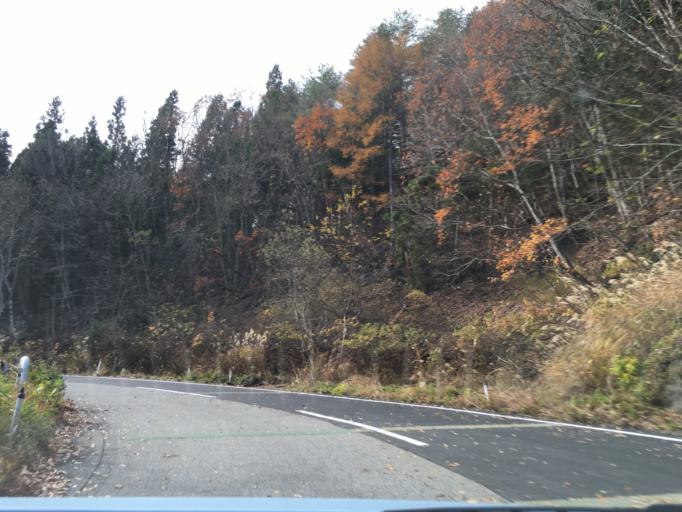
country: JP
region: Fukushima
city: Inawashiro
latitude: 37.4593
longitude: 140.0015
